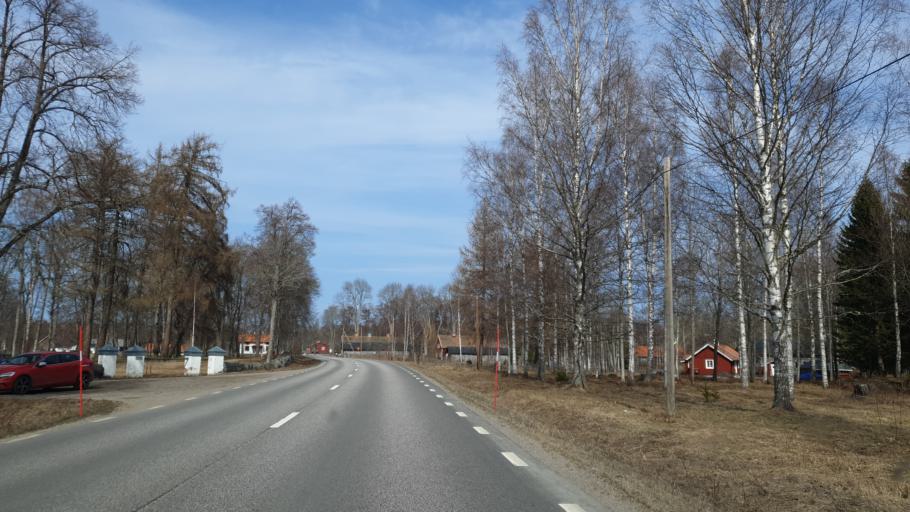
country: SE
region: Gaevleborg
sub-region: Gavle Kommun
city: Norrsundet
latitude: 61.0443
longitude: 17.1445
